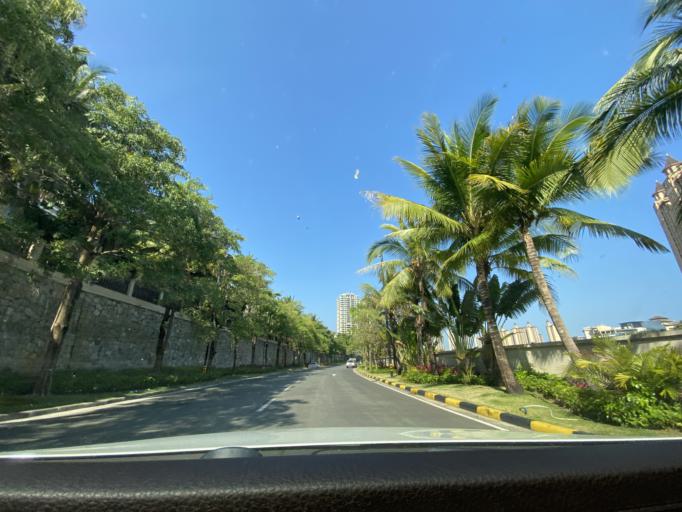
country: CN
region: Hainan
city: Yingzhou
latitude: 18.4088
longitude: 109.8773
